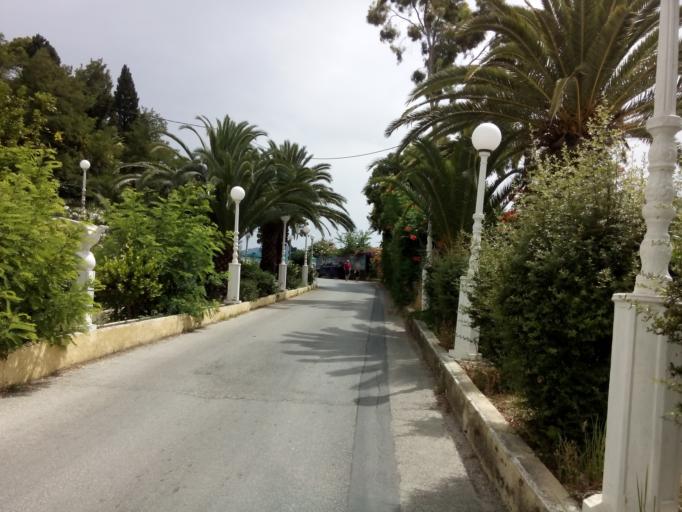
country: GR
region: Ionian Islands
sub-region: Nomos Kerkyras
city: Perama
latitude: 39.5925
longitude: 19.9173
